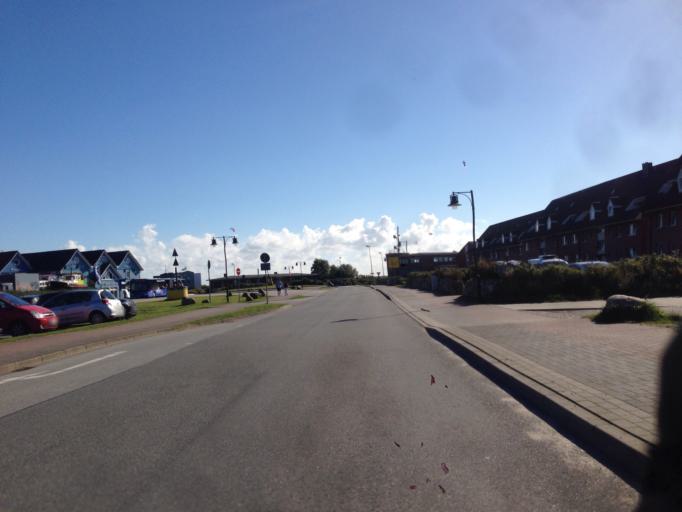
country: DE
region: Schleswig-Holstein
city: List
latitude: 55.0187
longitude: 8.4373
